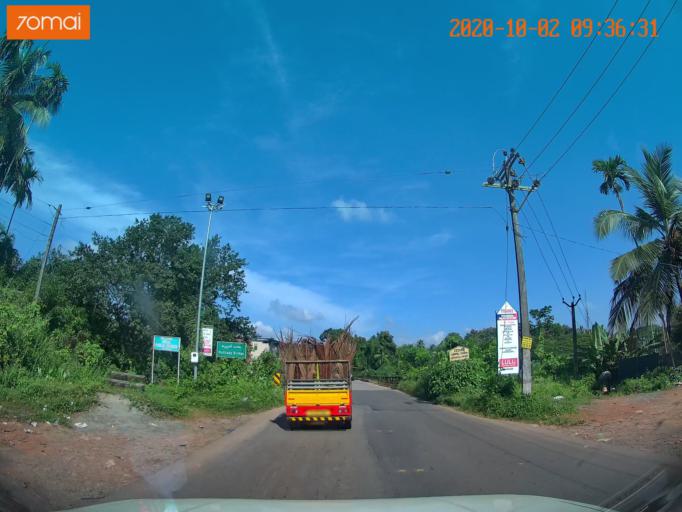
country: IN
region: Kerala
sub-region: Kozhikode
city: Nadapuram
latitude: 11.6496
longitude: 75.7555
